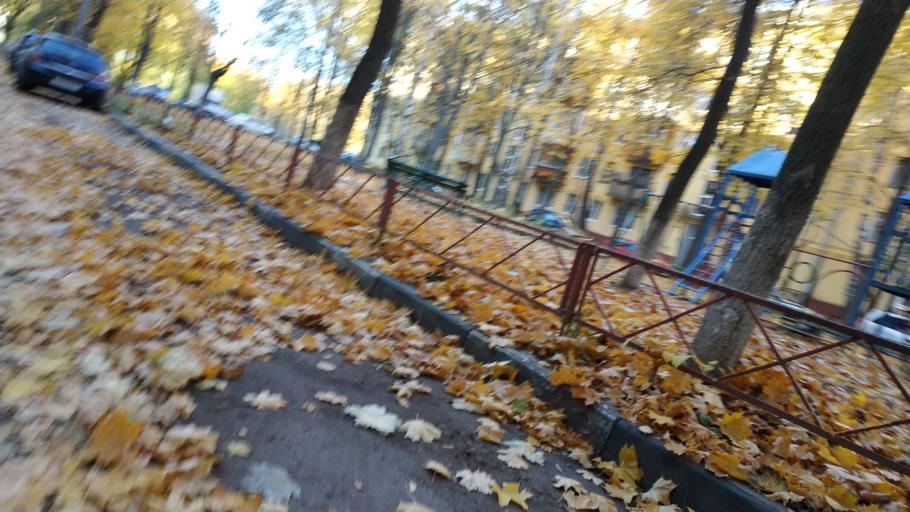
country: RU
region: Moskovskaya
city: Lobnya
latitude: 56.0091
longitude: 37.4604
